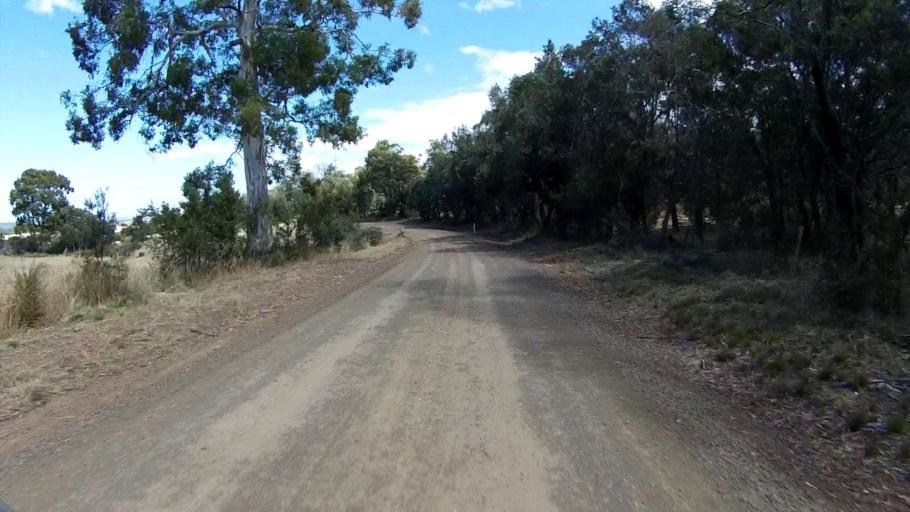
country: AU
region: Tasmania
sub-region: Break O'Day
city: St Helens
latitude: -41.9830
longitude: 148.0655
